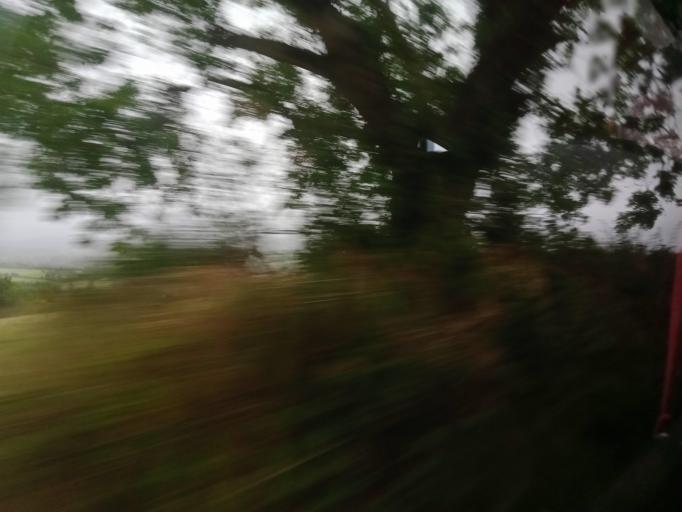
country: IE
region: Munster
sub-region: Waterford
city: Dungarvan
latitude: 52.0498
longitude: -7.6509
